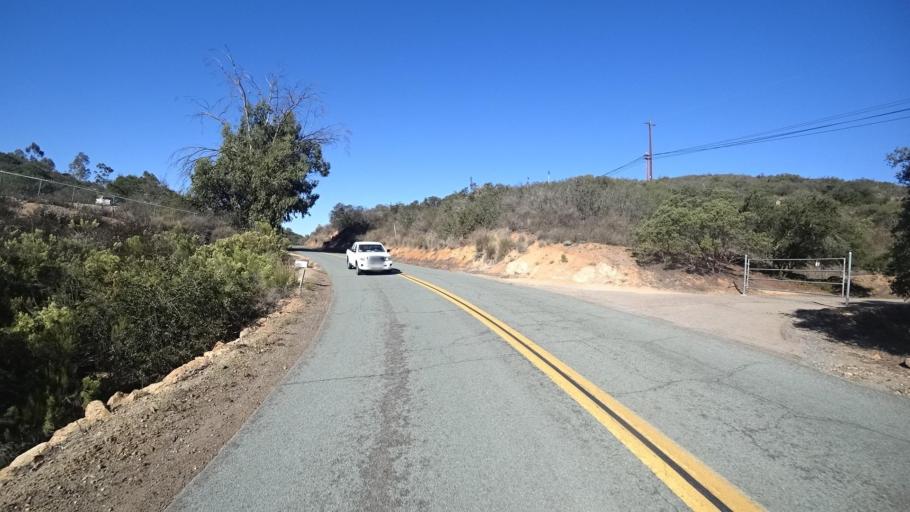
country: US
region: California
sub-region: San Diego County
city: Jamul
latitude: 32.7293
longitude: -116.8252
